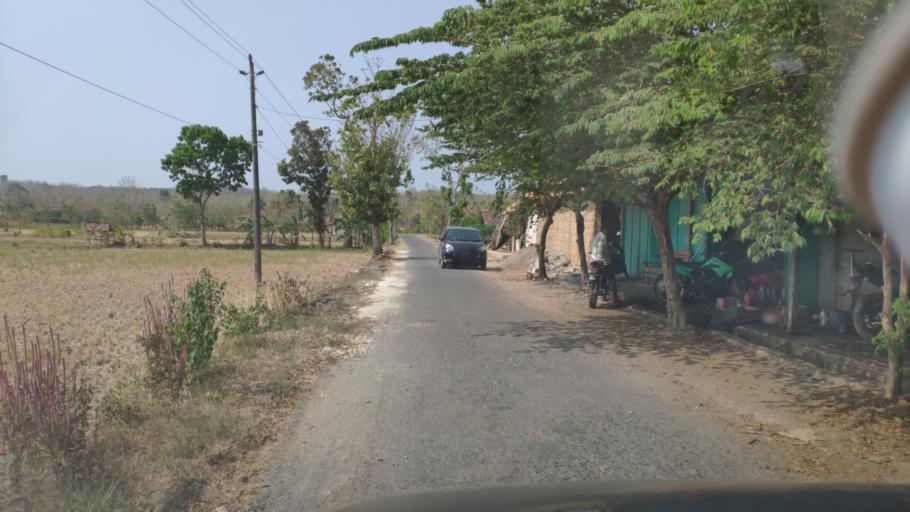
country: ID
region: Central Java
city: Tempuran
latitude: -6.9134
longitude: 111.4554
